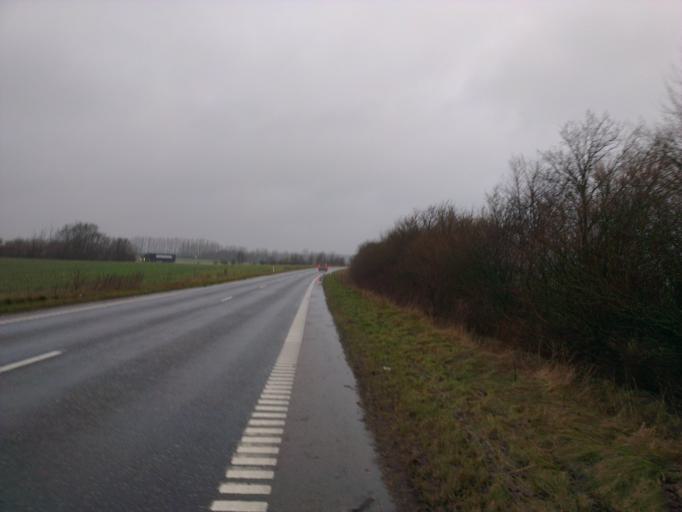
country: DK
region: Capital Region
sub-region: Frederikssund Kommune
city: Jaegerspris
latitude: 55.8261
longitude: 12.0138
